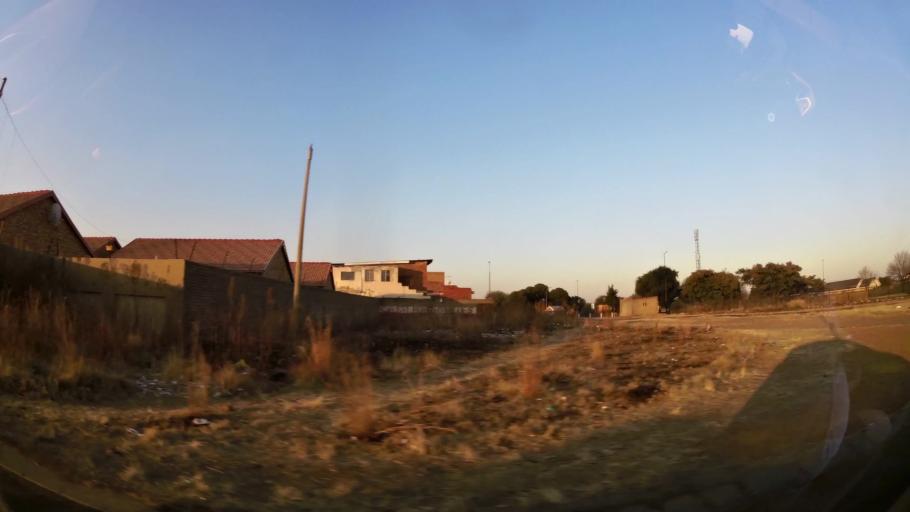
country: ZA
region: Gauteng
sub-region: West Rand District Municipality
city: Randfontein
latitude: -26.2045
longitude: 27.7049
